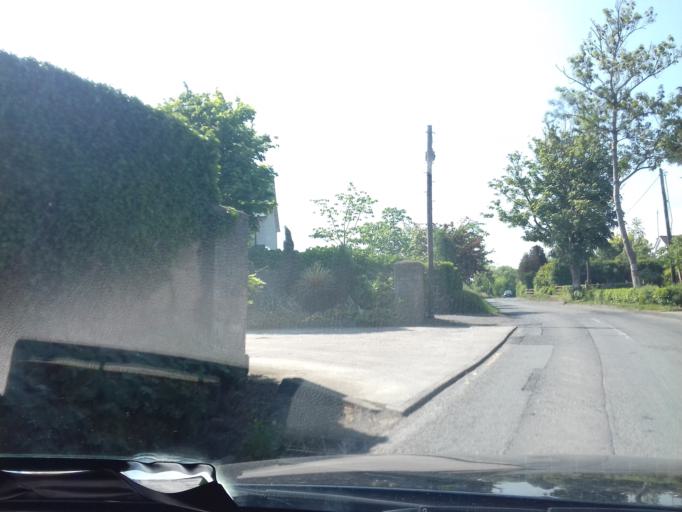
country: IE
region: Leinster
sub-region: Fingal County
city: Swords
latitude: 53.5119
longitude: -6.2236
